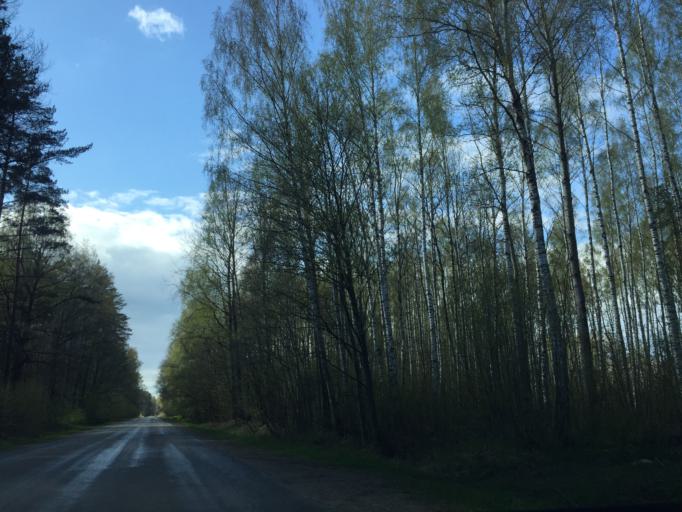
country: LV
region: Jelgava
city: Jelgava
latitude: 56.5695
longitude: 23.7451
